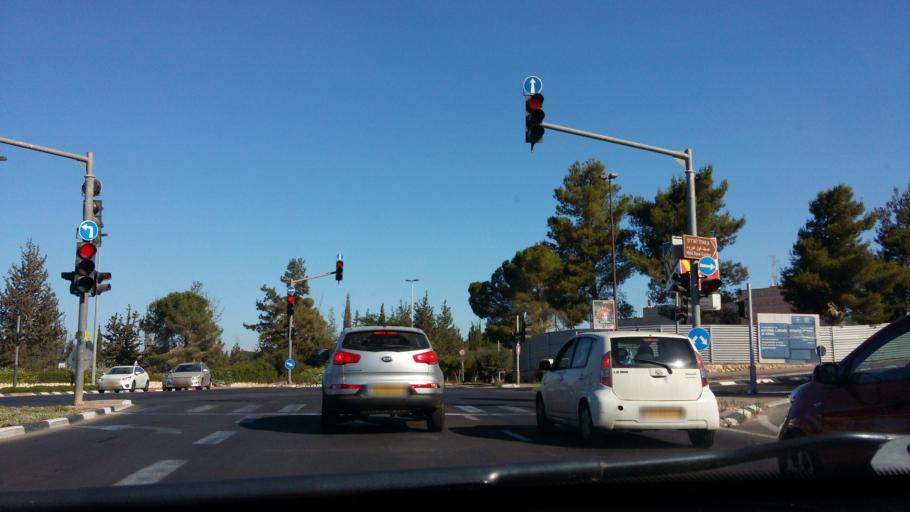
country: IL
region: Jerusalem
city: Jerusalem
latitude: 31.7748
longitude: 35.2045
